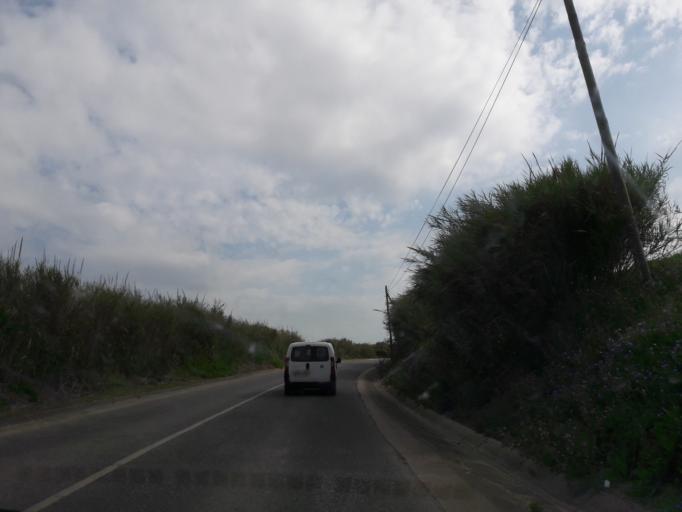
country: PT
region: Leiria
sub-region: Peniche
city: Atouguia da Baleia
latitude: 39.3550
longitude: -9.3196
